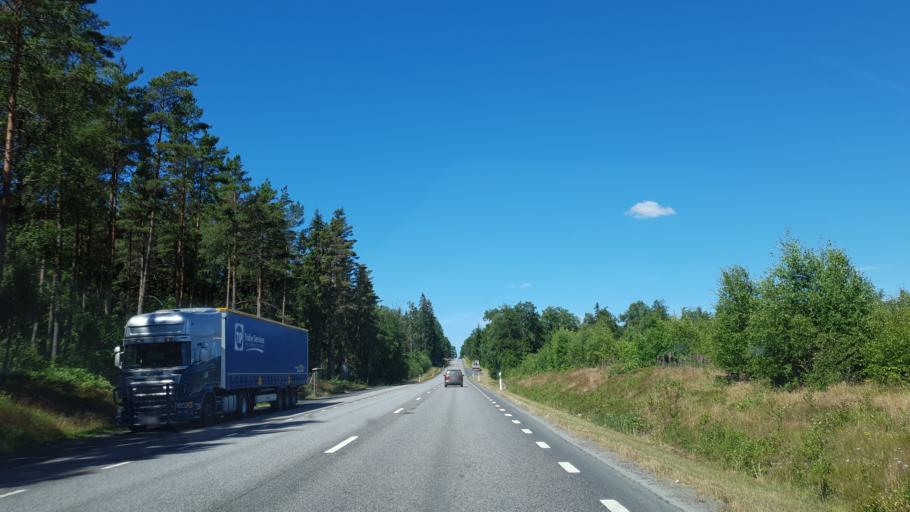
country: SE
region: Joenkoeping
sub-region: Varnamo Kommun
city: Bor
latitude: 57.1219
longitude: 14.1530
